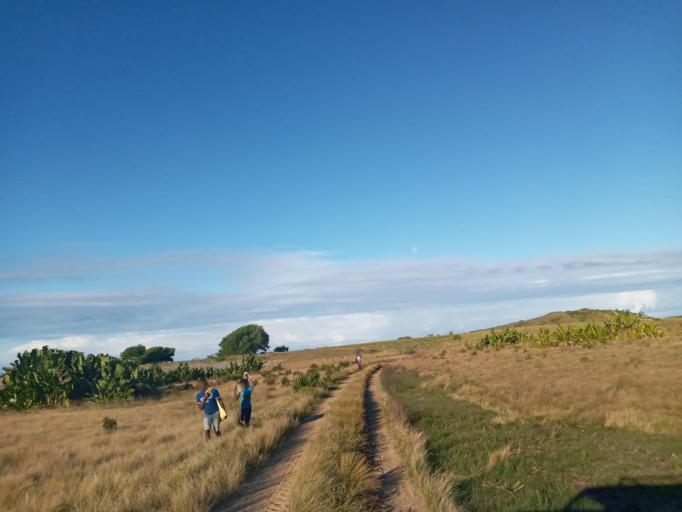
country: MG
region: Anosy
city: Fort Dauphin
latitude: -24.4314
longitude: 47.2983
